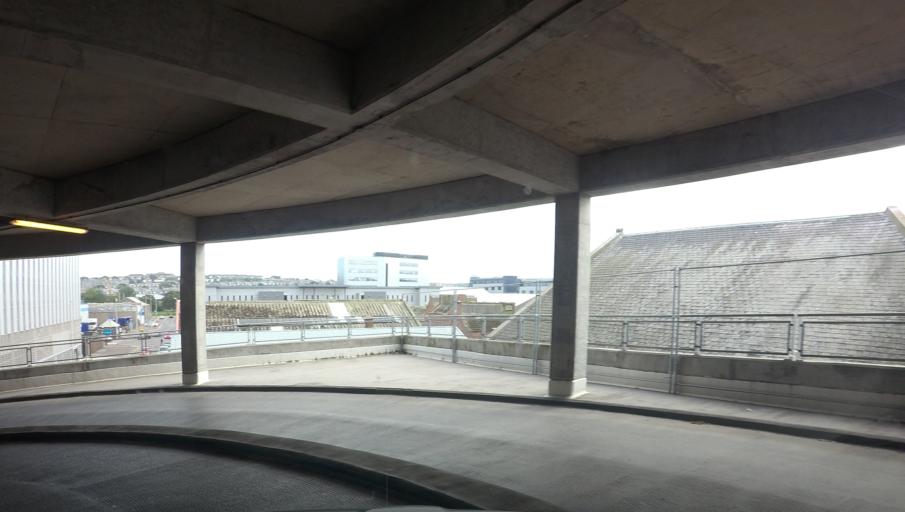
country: GB
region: Scotland
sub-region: Aberdeen City
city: Aberdeen
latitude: 57.1418
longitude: -2.0953
